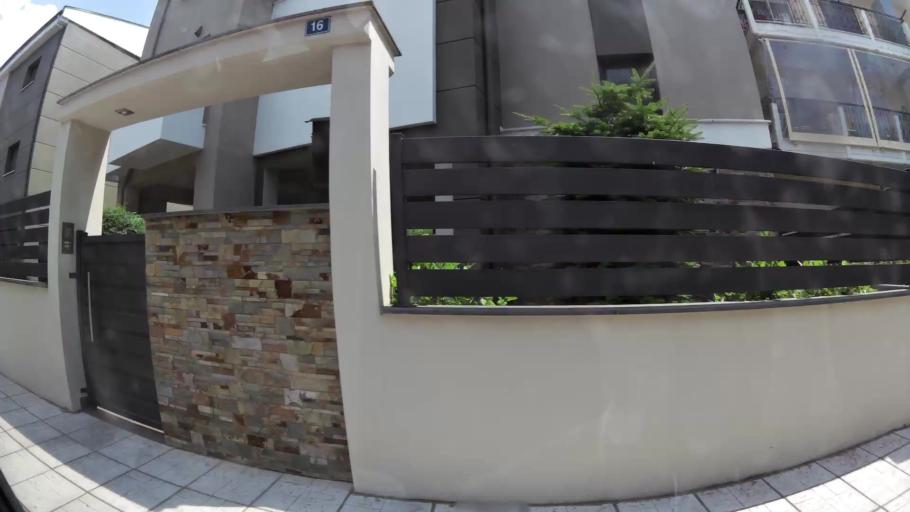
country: GR
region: West Macedonia
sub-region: Nomos Kozanis
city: Kozani
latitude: 40.3098
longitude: 21.7866
